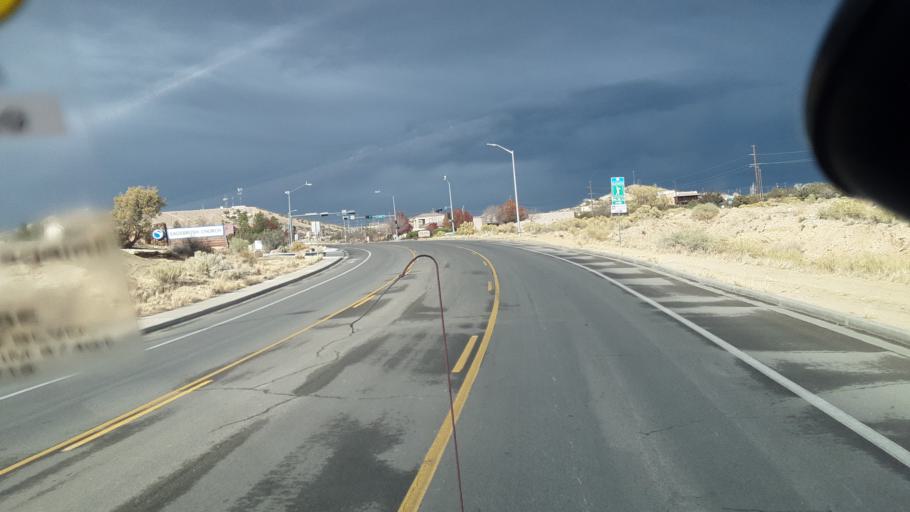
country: US
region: New Mexico
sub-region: San Juan County
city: Farmington
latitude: 36.7684
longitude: -108.1854
